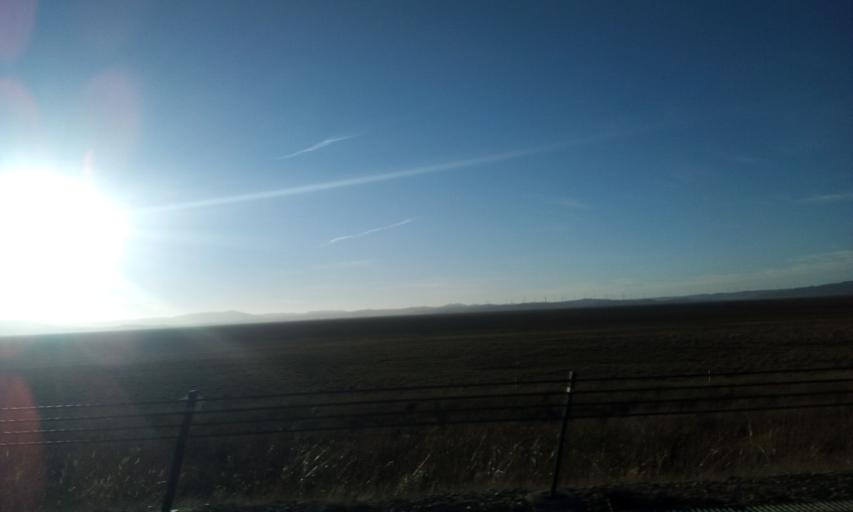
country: AU
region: New South Wales
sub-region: Yass Valley
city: Gundaroo
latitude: -35.0621
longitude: 149.3738
